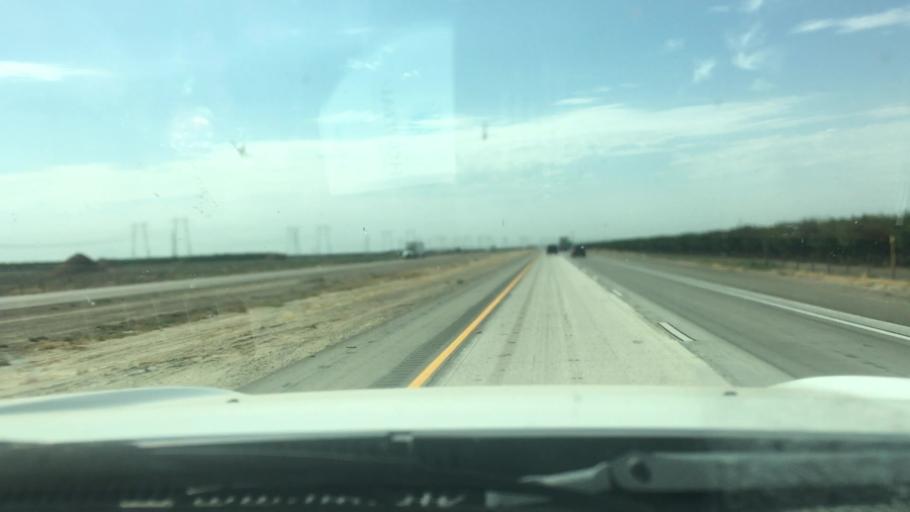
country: US
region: California
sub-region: Kern County
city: Buttonwillow
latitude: 35.5186
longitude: -119.5553
